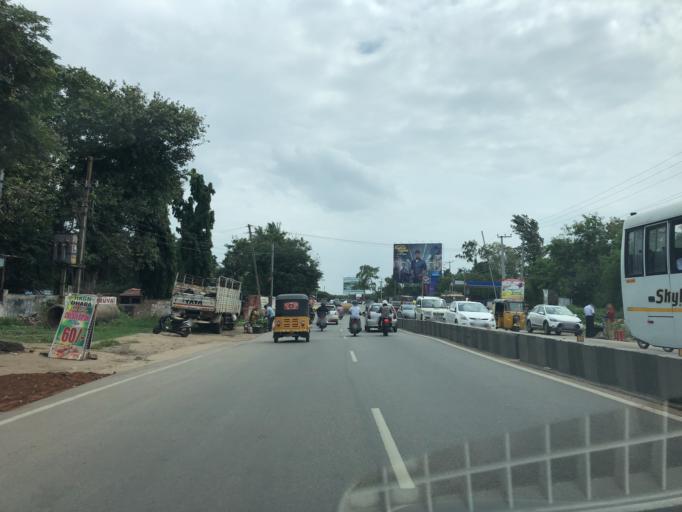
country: IN
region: Telangana
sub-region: Rangareddi
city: Quthbullapur
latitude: 17.4749
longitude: 78.4740
